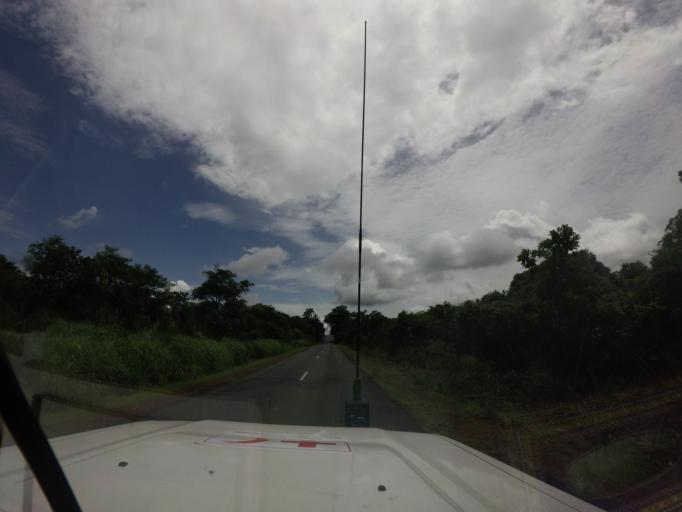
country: GN
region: Faranah
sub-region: Faranah Prefecture
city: Faranah
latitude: 10.0166
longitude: -10.9523
